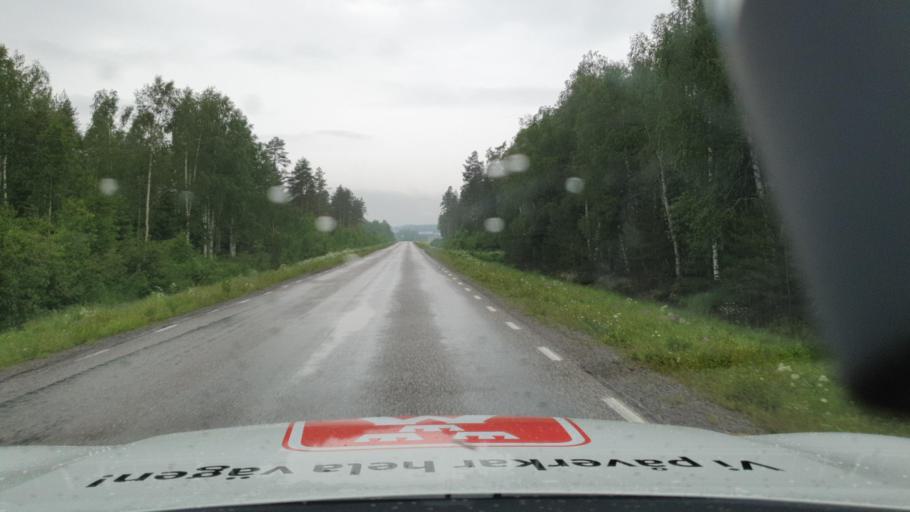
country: SE
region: Vaesterbotten
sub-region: Vannas Kommun
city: Vaennaes
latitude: 63.7840
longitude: 19.5846
